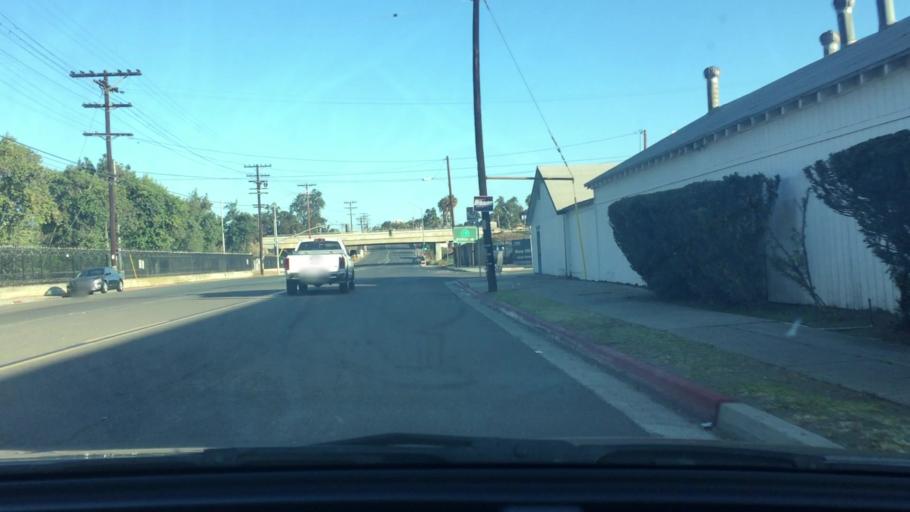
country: US
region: California
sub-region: San Diego County
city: National City
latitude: 32.6899
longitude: -117.1216
